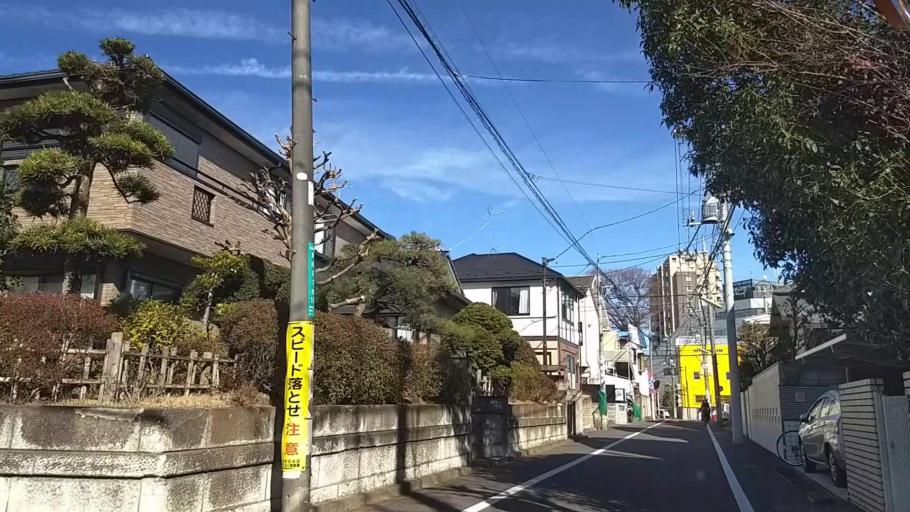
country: JP
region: Tokyo
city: Chofugaoka
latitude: 35.6228
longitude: 139.6268
